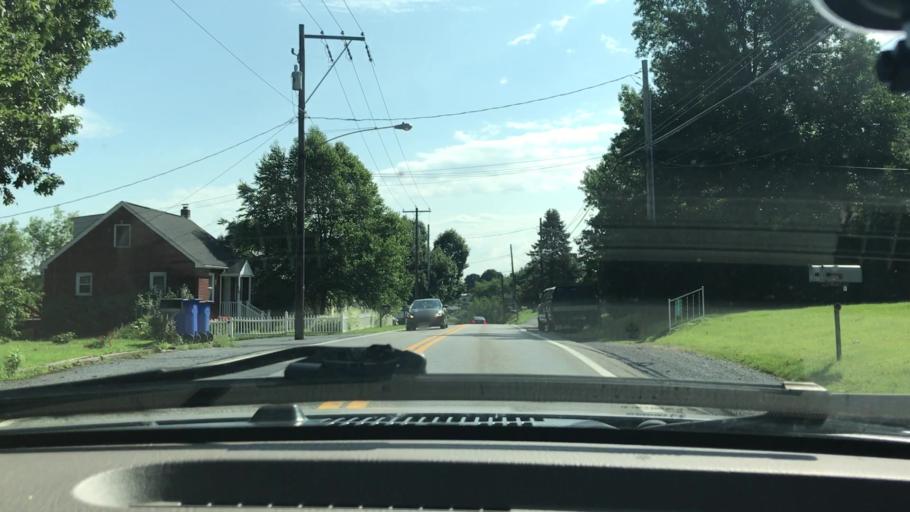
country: US
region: Pennsylvania
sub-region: Dauphin County
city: Rutherford
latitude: 40.2607
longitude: -76.7466
